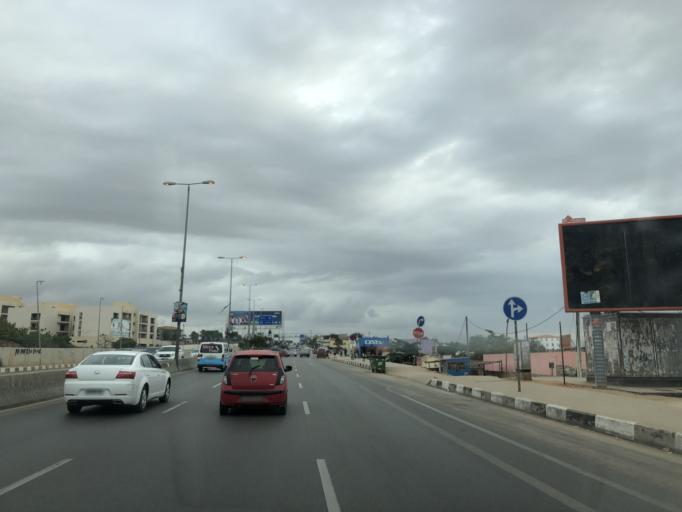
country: AO
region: Luanda
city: Luanda
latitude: -8.8655
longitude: 13.2135
